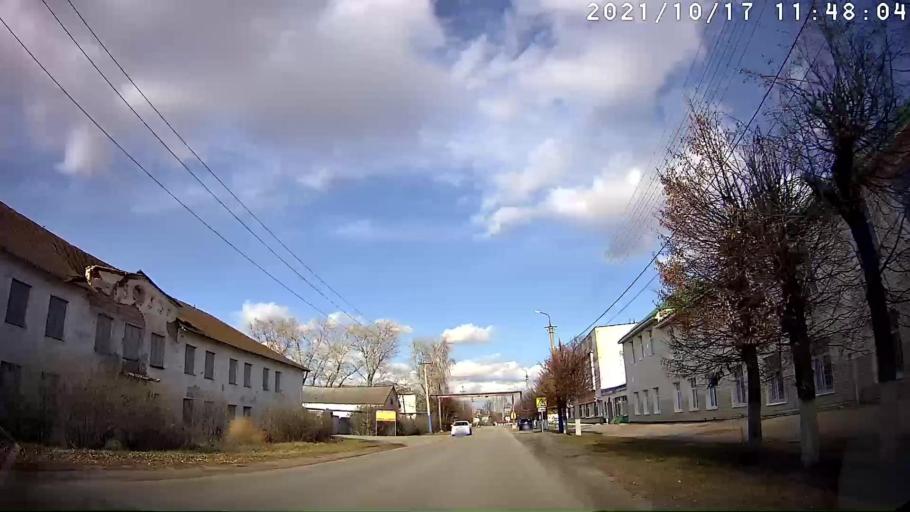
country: RU
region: Mariy-El
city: Kuzhener
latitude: 57.0018
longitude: 48.7337
